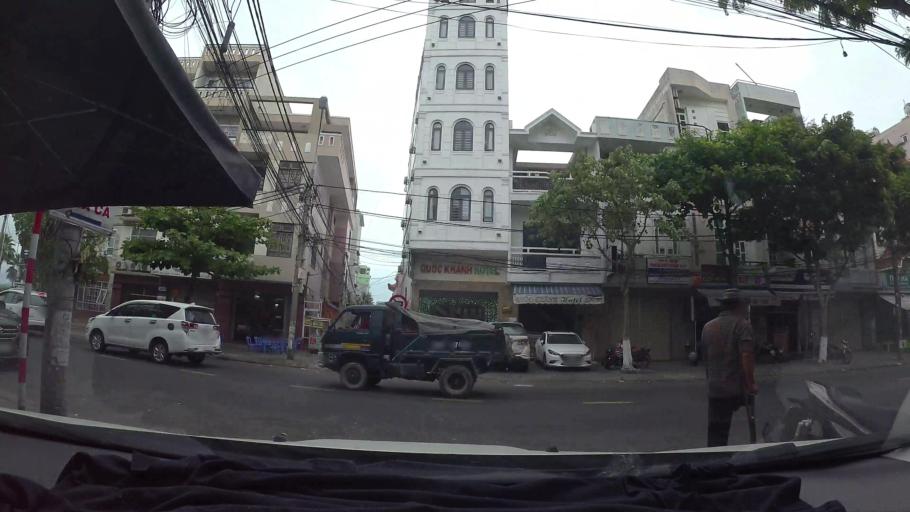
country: VN
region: Da Nang
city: Thanh Khe
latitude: 16.0726
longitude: 108.2011
